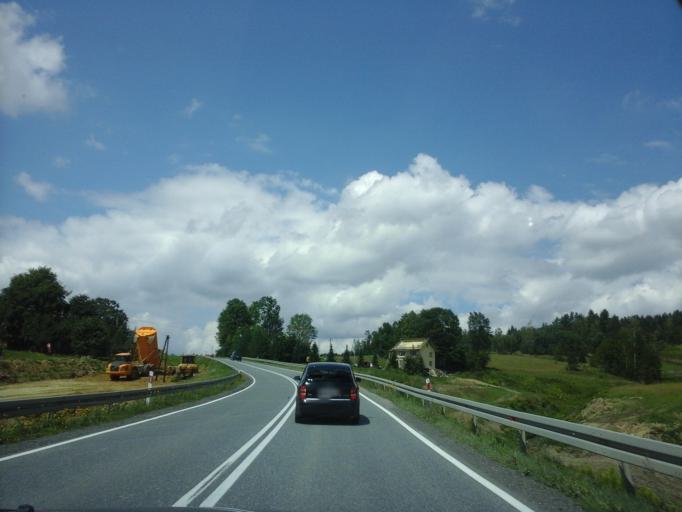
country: PL
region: Lesser Poland Voivodeship
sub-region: Powiat suski
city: Naprawa
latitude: 49.6477
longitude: 19.9058
